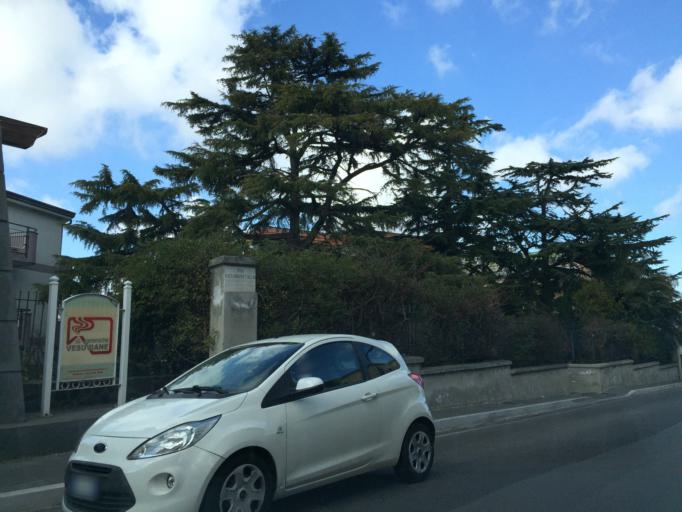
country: IT
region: Campania
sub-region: Provincia di Napoli
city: Massa di Somma
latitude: 40.8456
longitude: 14.3728
